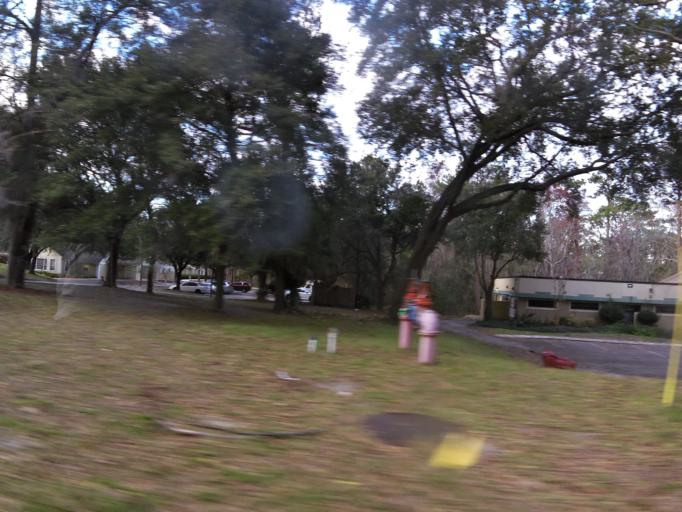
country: US
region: Florida
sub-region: Duval County
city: Jacksonville
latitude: 30.2901
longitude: -81.7189
